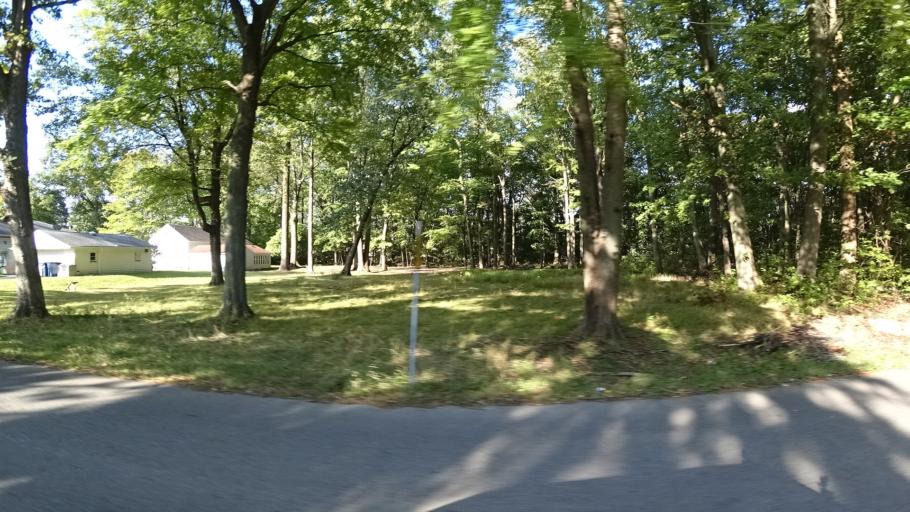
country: US
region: Indiana
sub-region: LaPorte County
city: Trail Creek
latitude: 41.6953
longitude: -86.8647
